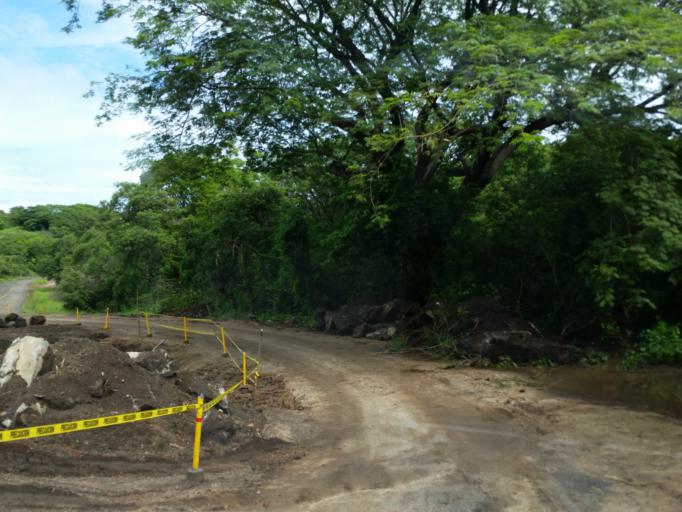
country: NI
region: Leon
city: La Paz Centro
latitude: 12.3598
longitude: -86.6634
